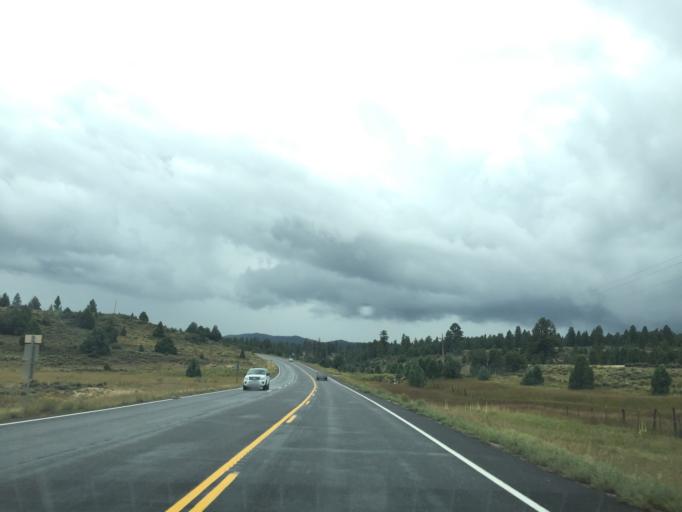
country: US
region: Utah
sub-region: Garfield County
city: Panguitch
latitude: 37.4844
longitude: -112.5142
